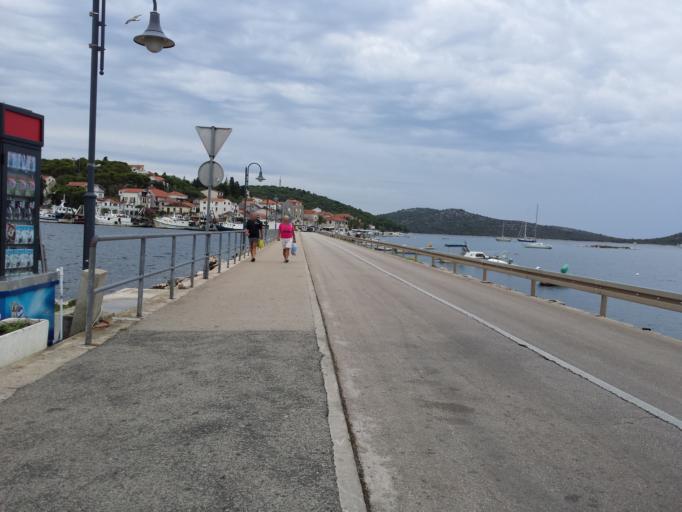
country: HR
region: Sibensko-Kniniska
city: Rogoznica
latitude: 43.5319
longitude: 15.9677
